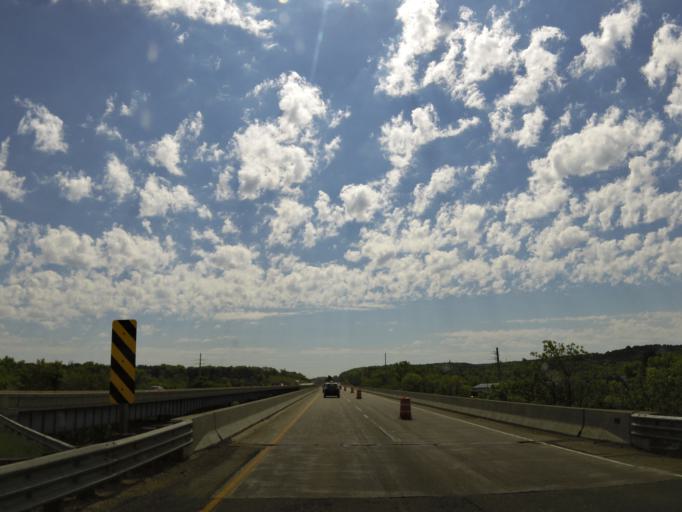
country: US
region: Wisconsin
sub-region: Eau Claire County
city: Eau Claire
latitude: 44.7813
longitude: -91.5395
